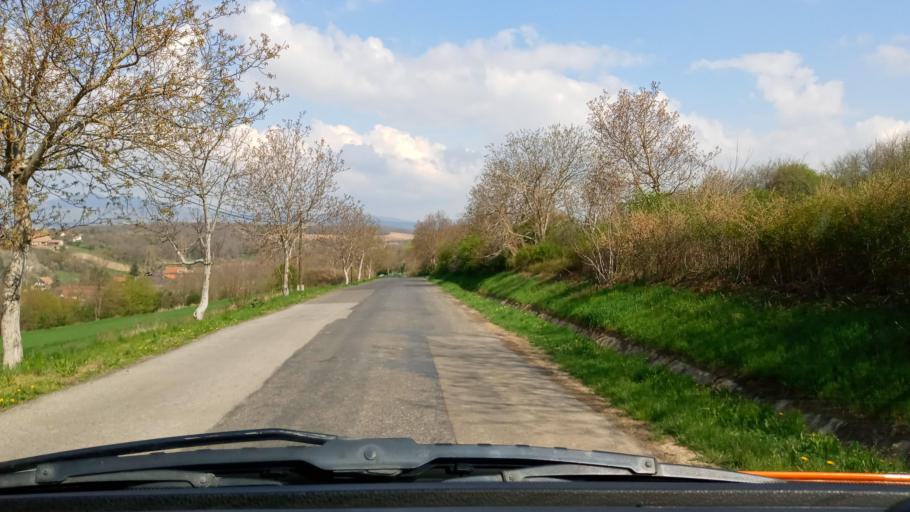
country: HU
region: Baranya
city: Pecsvarad
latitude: 46.0975
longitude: 18.4628
